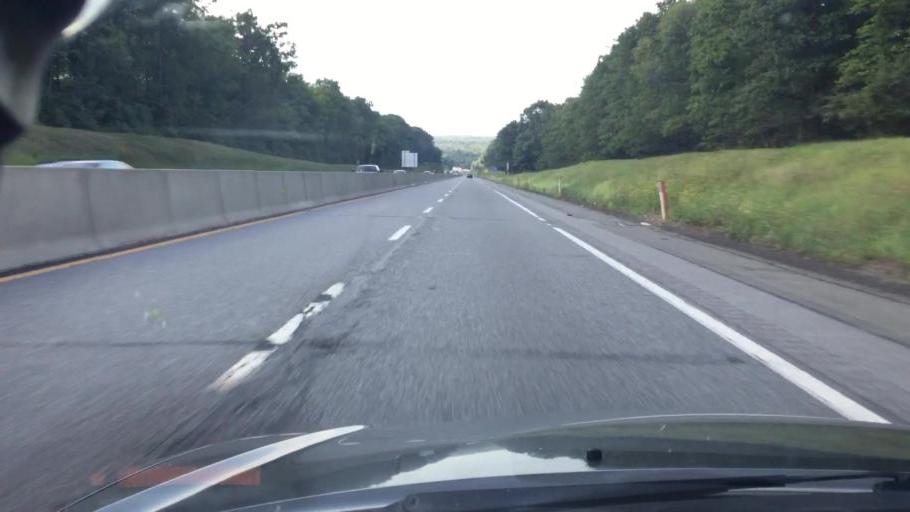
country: US
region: Pennsylvania
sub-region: Carbon County
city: Towamensing Trails
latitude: 40.9968
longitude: -75.6330
